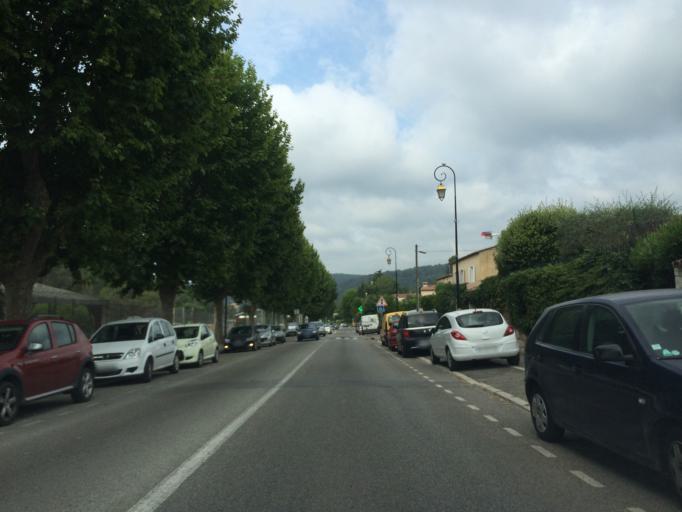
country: FR
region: Provence-Alpes-Cote d'Azur
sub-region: Departement des Alpes-Maritimes
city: La Colle-sur-Loup
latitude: 43.6860
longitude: 7.1016
